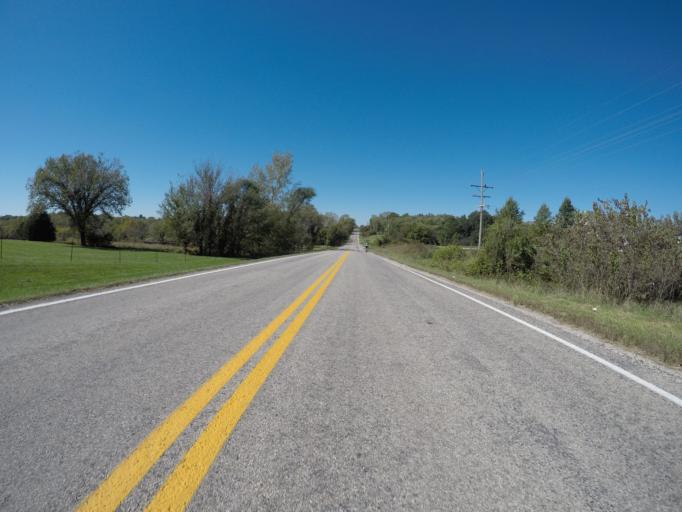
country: US
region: Kansas
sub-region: Johnson County
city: De Soto
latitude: 39.0146
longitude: -94.9351
